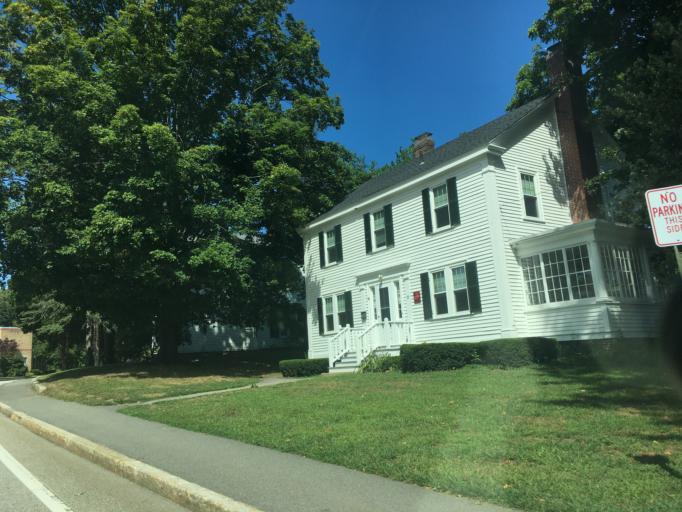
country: US
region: New Hampshire
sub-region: Rockingham County
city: Exeter
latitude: 42.9816
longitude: -70.9529
